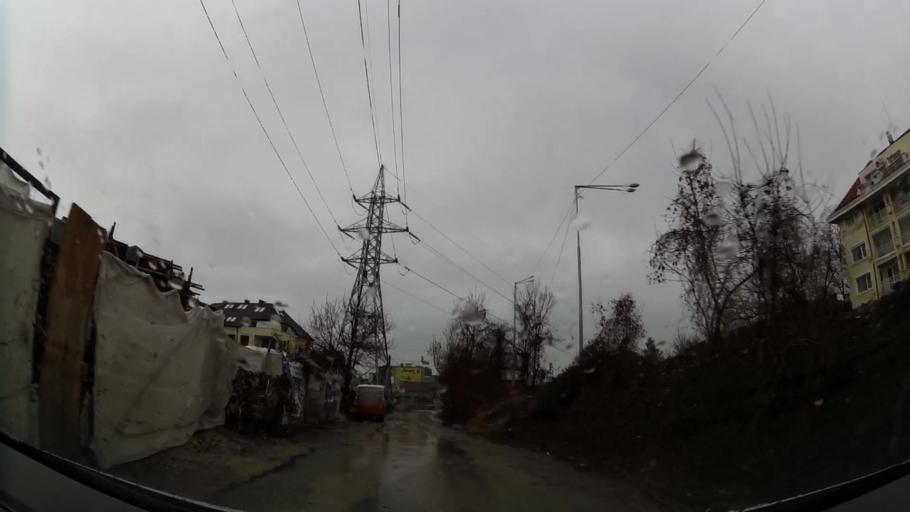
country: BG
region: Sofia-Capital
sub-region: Stolichna Obshtina
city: Sofia
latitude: 42.6448
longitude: 23.3335
